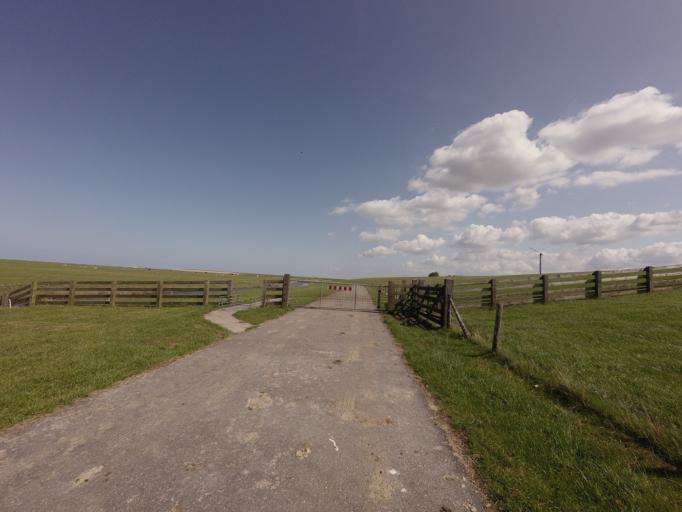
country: NL
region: Friesland
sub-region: Gemeente Ferwerderadiel
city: Ferwert
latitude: 53.3626
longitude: 5.8489
